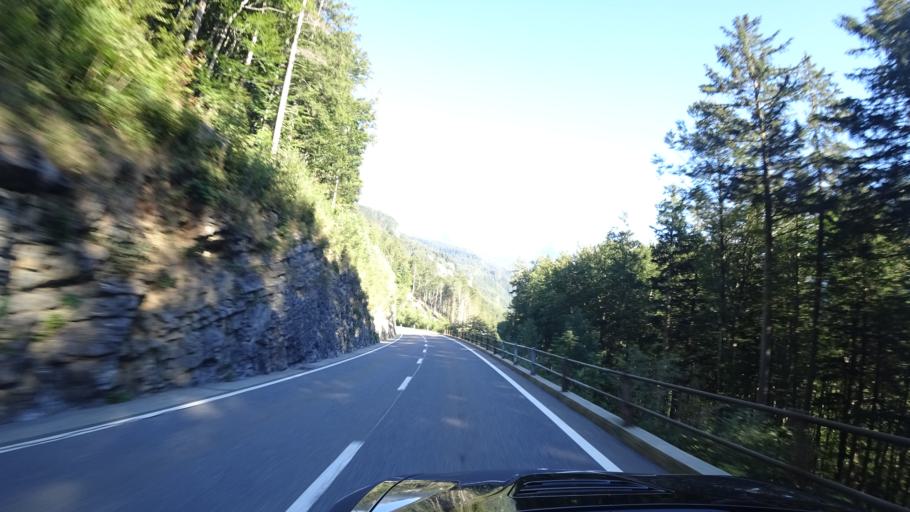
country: CH
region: Obwalden
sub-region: Obwalden
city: Lungern
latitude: 46.7472
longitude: 8.1476
